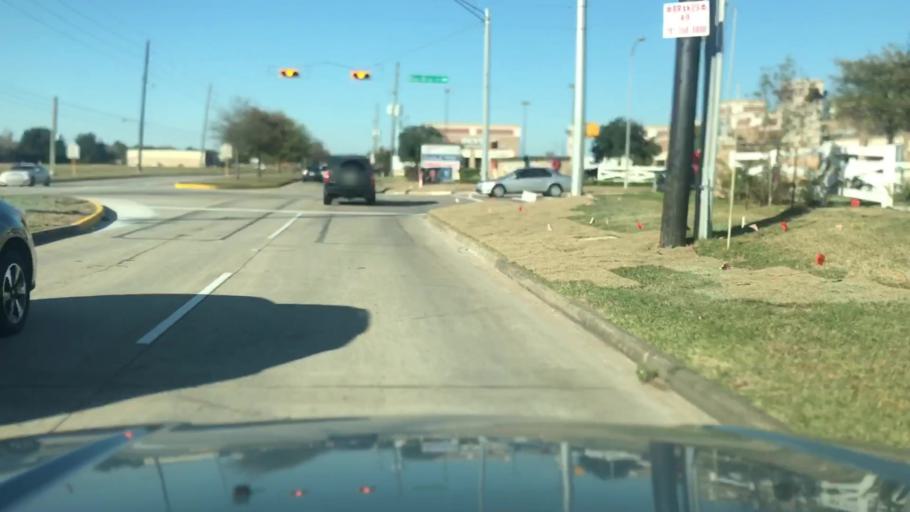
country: US
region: Texas
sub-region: Fort Bend County
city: Cinco Ranch
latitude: 29.8128
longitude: -95.7521
